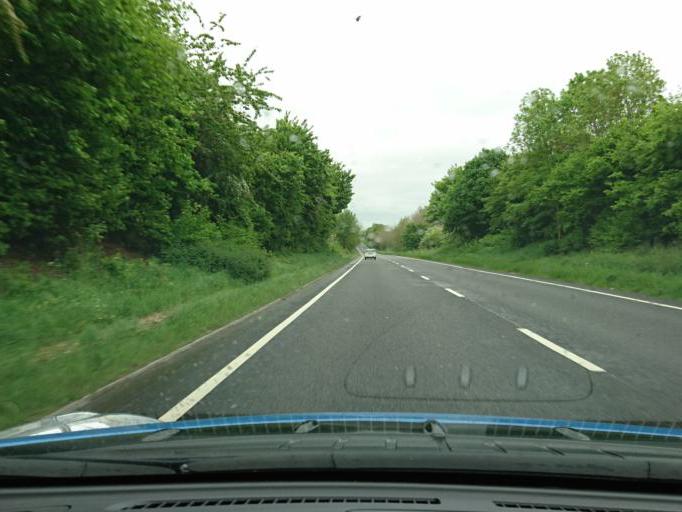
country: GB
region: England
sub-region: Oxfordshire
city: Shrivenham
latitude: 51.6080
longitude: -1.6584
